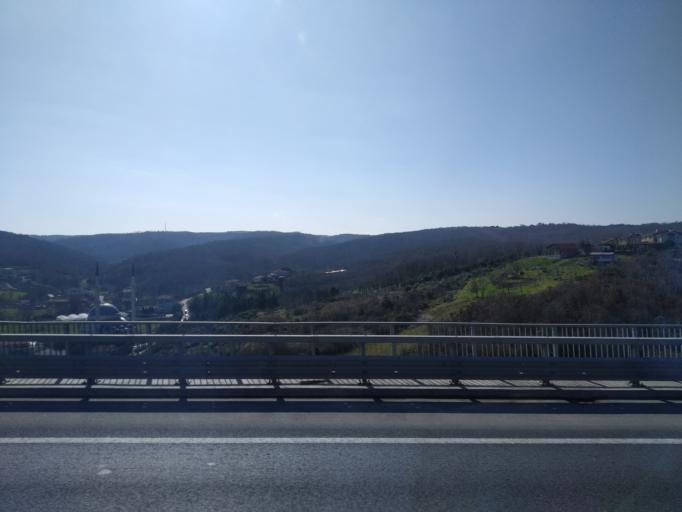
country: TR
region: Istanbul
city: Mahmut Sevket Pasa
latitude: 41.1820
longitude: 29.2320
